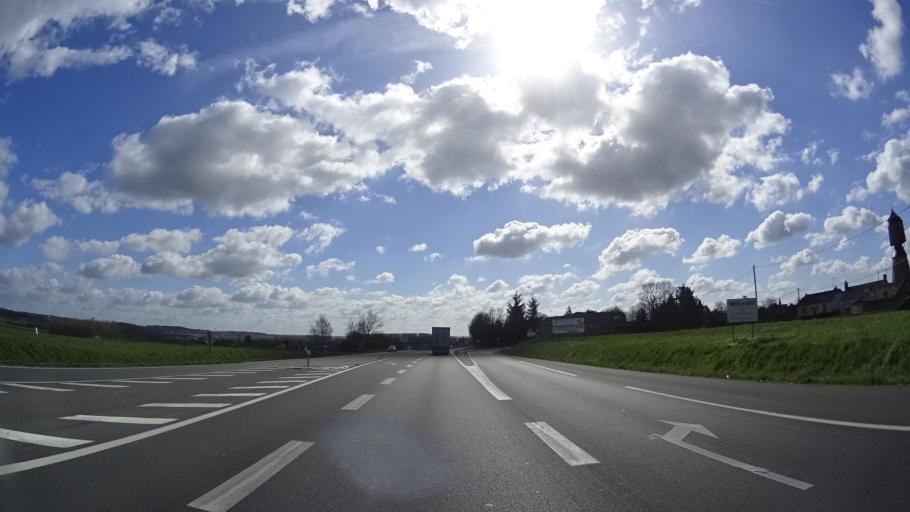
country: FR
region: Pays de la Loire
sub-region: Departement de Maine-et-Loire
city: Brissac-Quince
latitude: 47.3643
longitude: -0.4512
